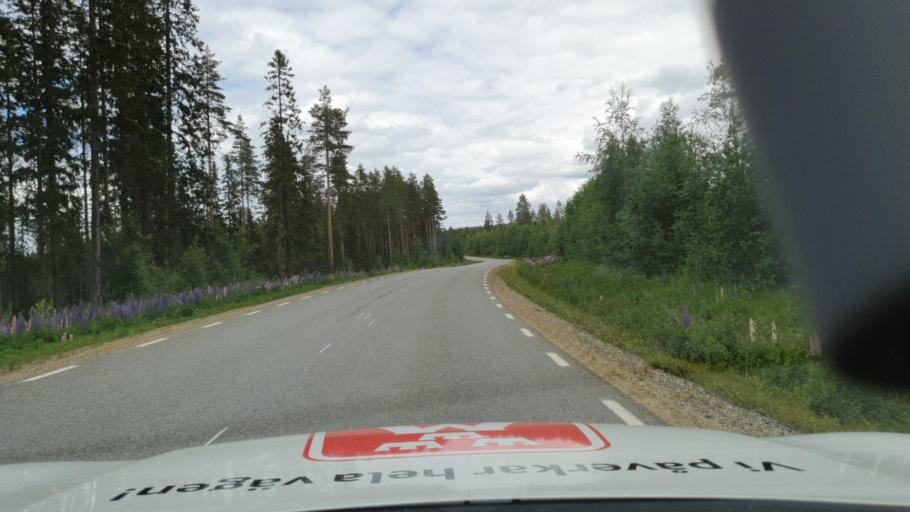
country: SE
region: Vaesterbotten
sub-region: Bjurholms Kommun
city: Bjurholm
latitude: 63.8756
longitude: 18.9850
